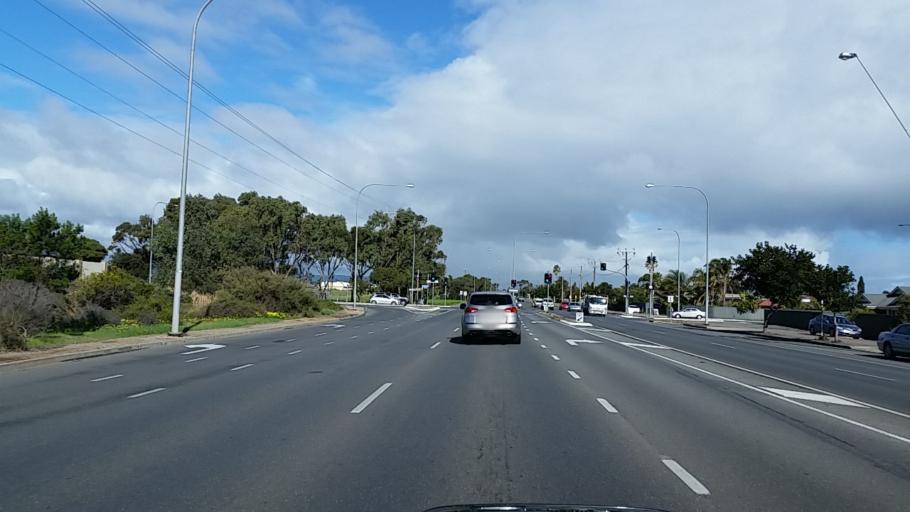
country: AU
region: South Australia
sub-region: Onkaparinga
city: Seaford
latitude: -35.1800
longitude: 138.4767
